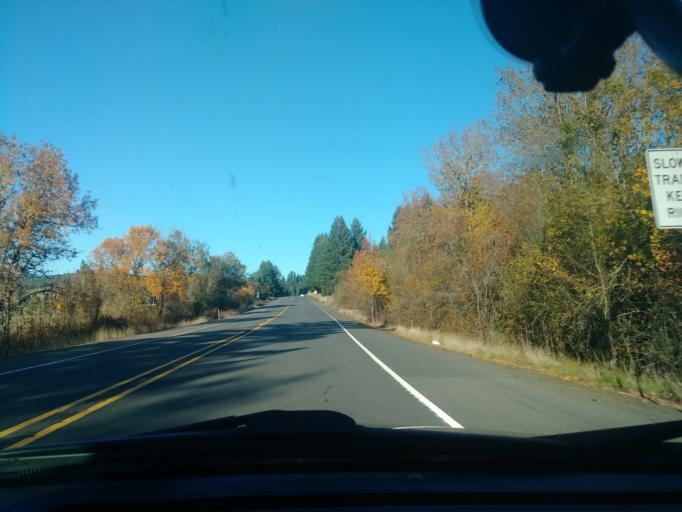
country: US
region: Oregon
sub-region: Washington County
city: Banks
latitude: 45.6125
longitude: -123.2288
